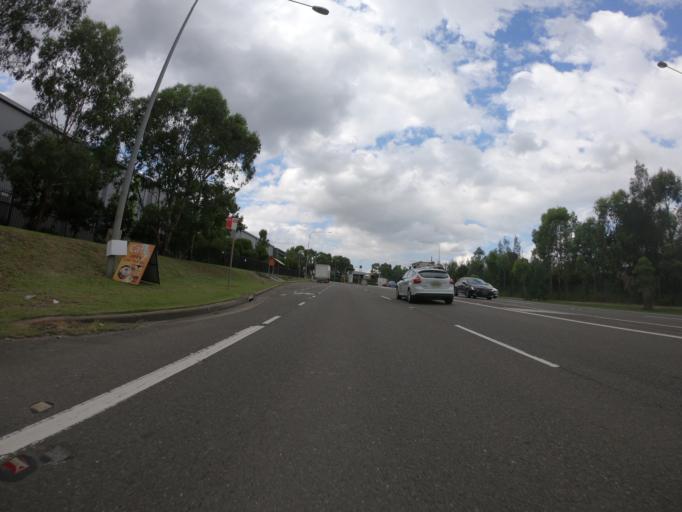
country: AU
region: New South Wales
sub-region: Blacktown
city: Mount Druitt
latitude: -33.8152
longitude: 150.7803
